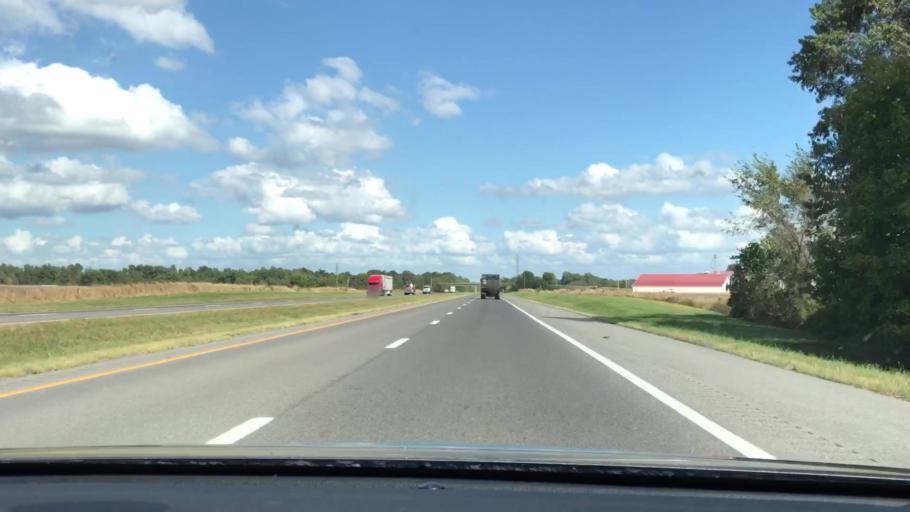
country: US
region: Kentucky
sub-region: Marshall County
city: Benton
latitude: 36.8252
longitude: -88.4646
